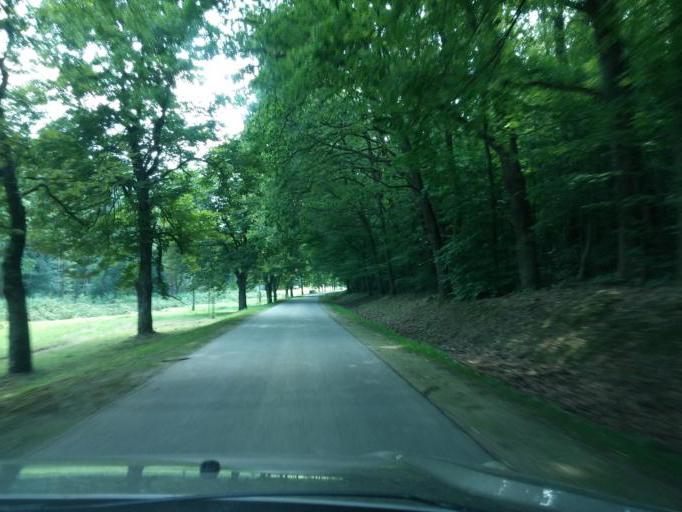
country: HU
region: Somogy
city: Kaposvar
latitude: 46.2502
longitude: 17.7782
